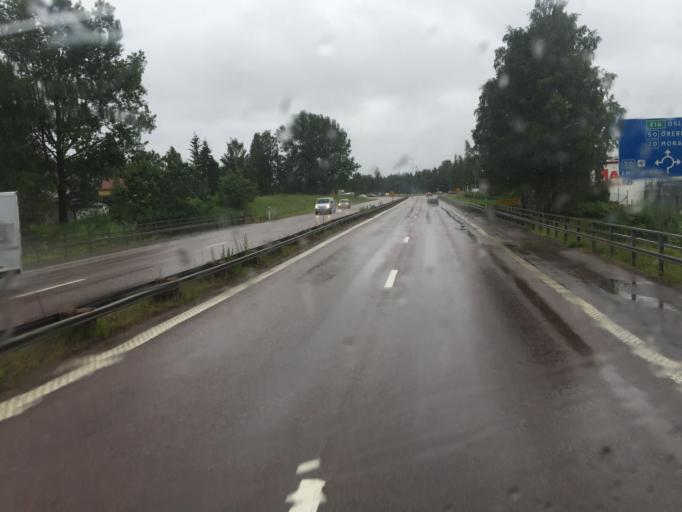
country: SE
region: Dalarna
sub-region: Borlange Kommun
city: Borlaenge
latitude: 60.4826
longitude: 15.4516
